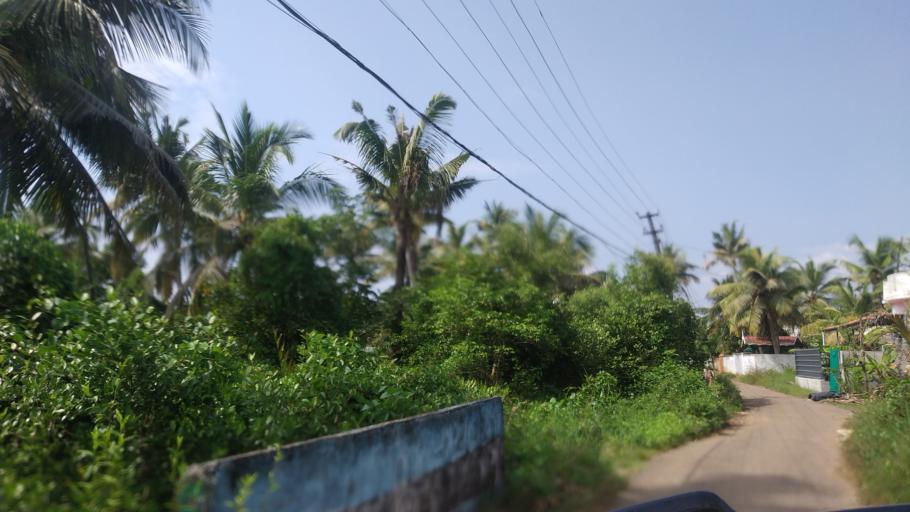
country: IN
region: Kerala
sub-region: Ernakulam
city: Elur
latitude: 10.0783
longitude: 76.2048
